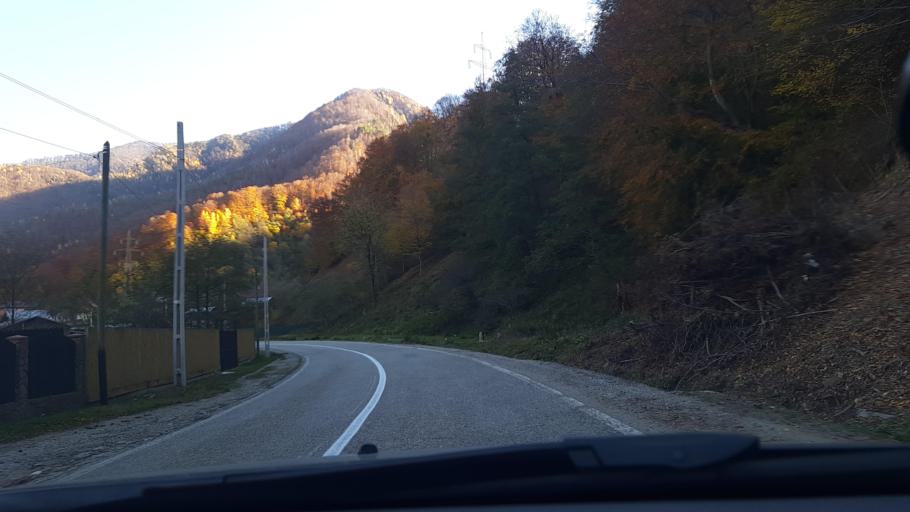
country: RO
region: Valcea
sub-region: Comuna Malaia
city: Malaia
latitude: 45.3550
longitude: 24.1271
